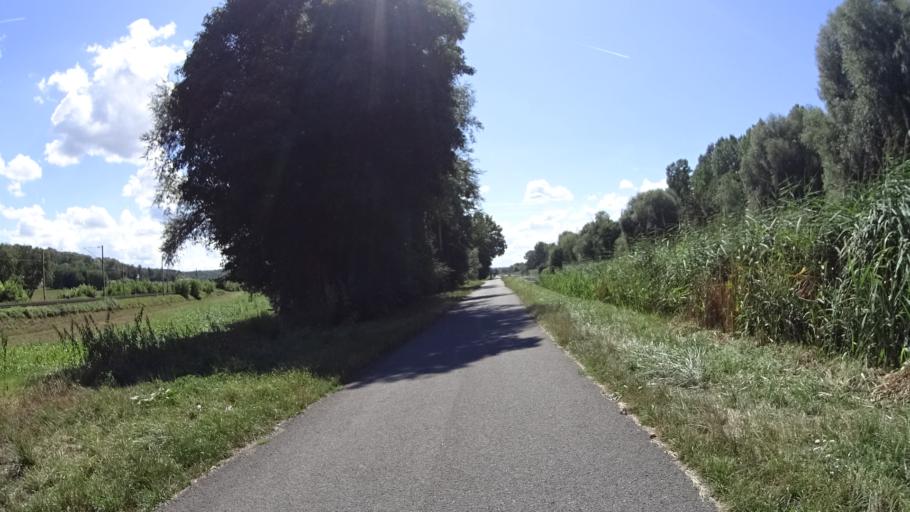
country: FR
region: Alsace
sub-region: Departement du Haut-Rhin
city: Flaxlanden
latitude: 47.7056
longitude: 7.3100
